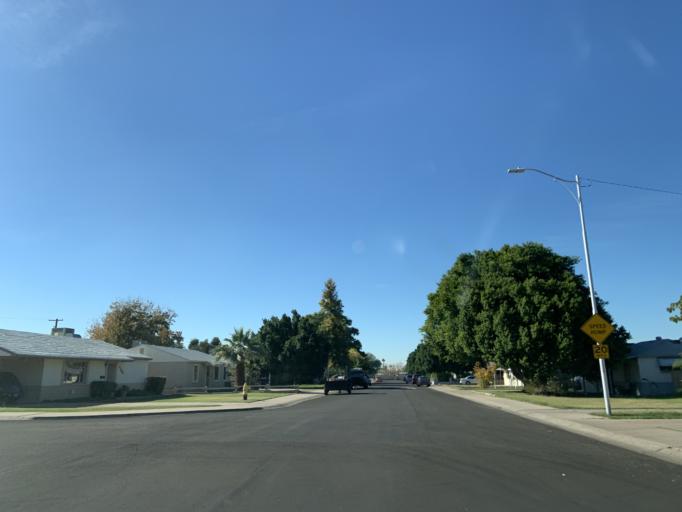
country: US
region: Arizona
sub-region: Maricopa County
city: Mesa
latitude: 33.4181
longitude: -111.8631
